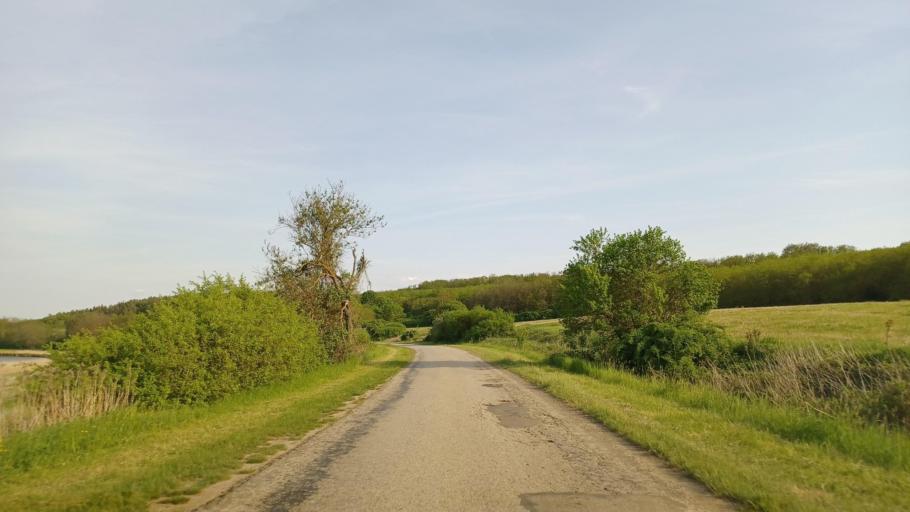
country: HU
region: Baranya
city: Kozarmisleny
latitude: 45.9659
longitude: 18.3669
